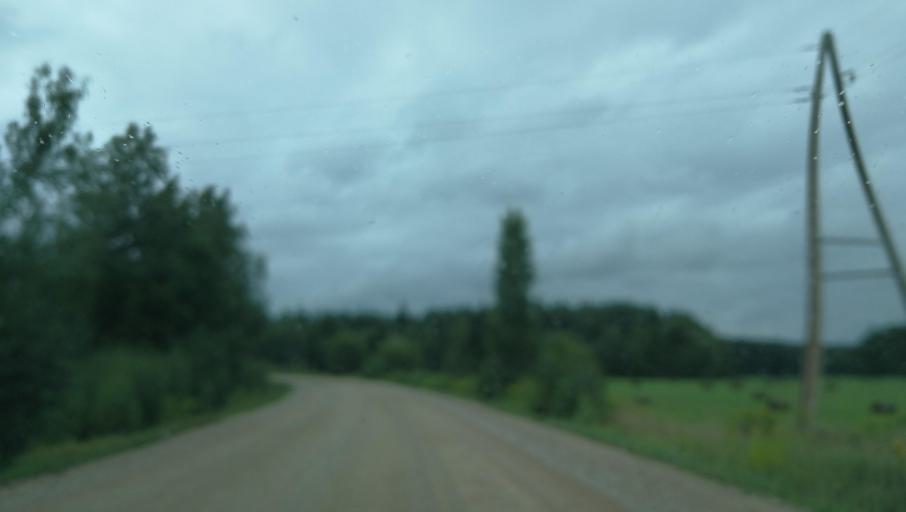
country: LV
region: Beverina
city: Murmuiza
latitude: 57.4164
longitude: 25.5149
